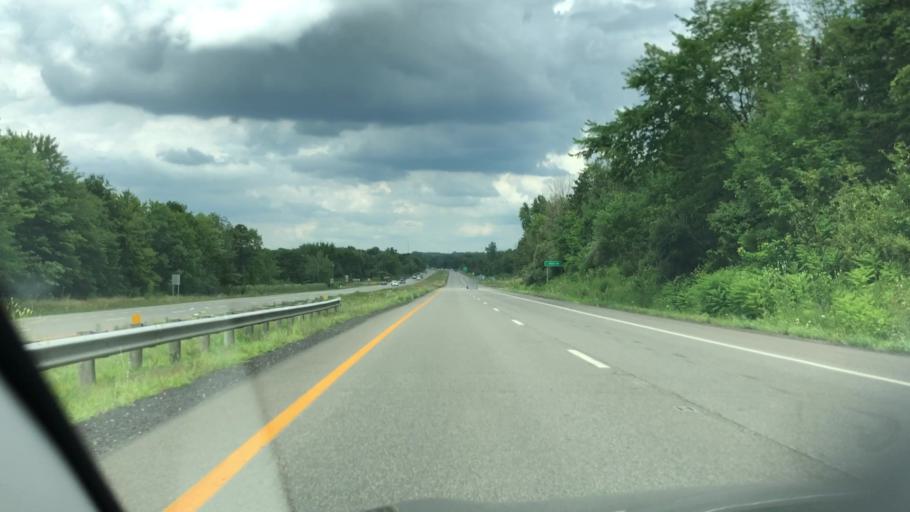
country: US
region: Ohio
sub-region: Summit County
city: Norton
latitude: 41.0785
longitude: -81.6652
